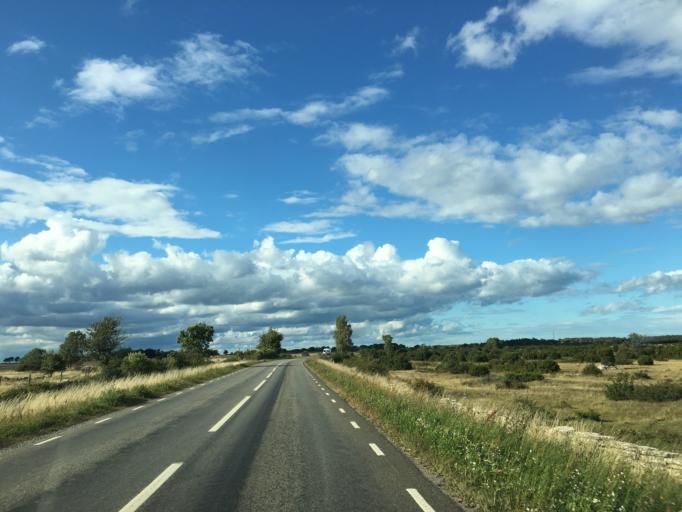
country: SE
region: Kalmar
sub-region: Morbylanga Kommun
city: Moerbylanga
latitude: 56.4942
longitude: 16.4261
